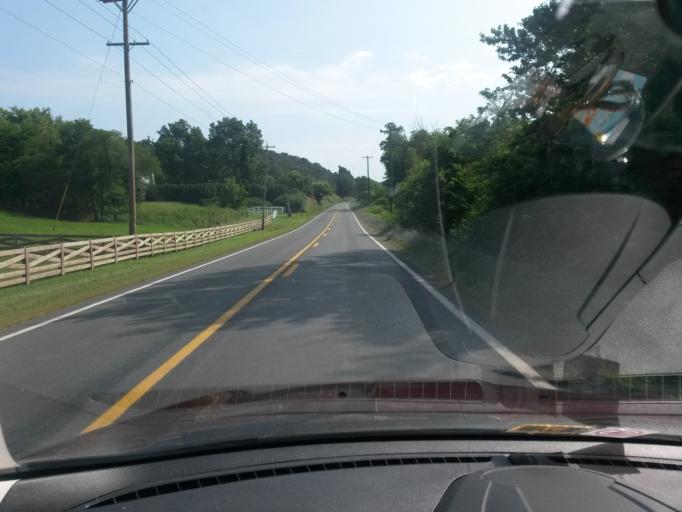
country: US
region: Virginia
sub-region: Shenandoah County
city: Basye
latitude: 38.9780
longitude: -78.7928
